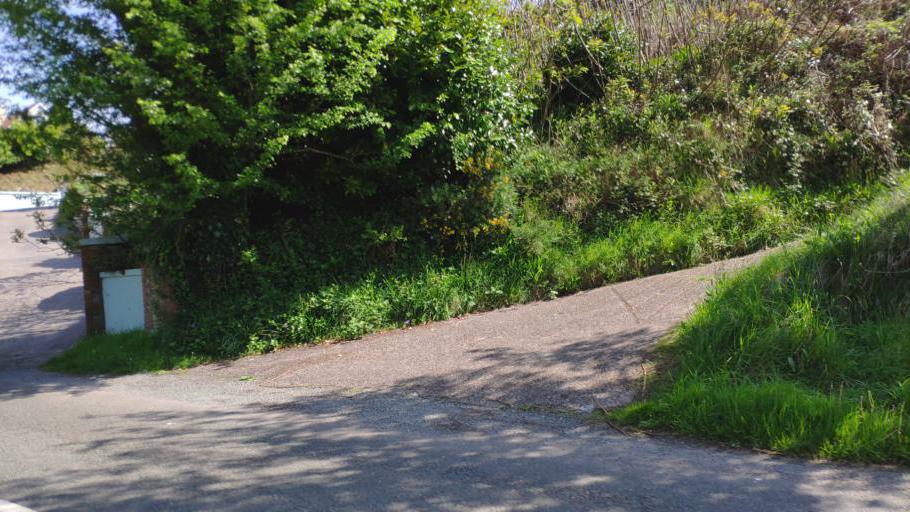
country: IE
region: Munster
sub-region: County Cork
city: Blarney
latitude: 51.9584
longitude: -8.5760
